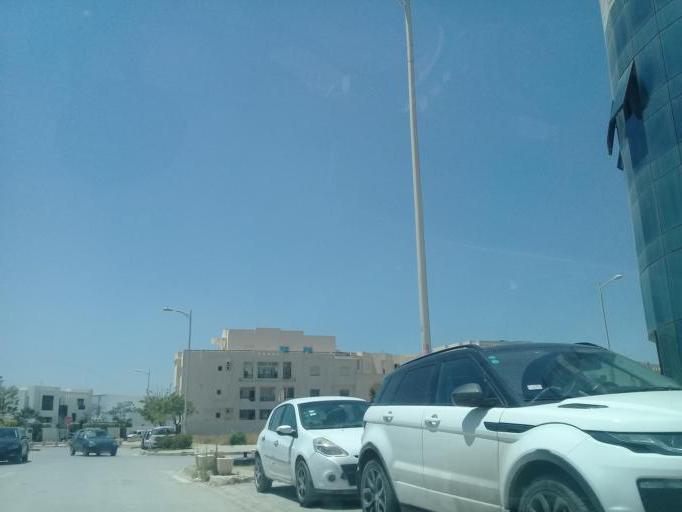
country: TN
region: Tunis
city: La Goulette
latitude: 36.8441
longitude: 10.2695
